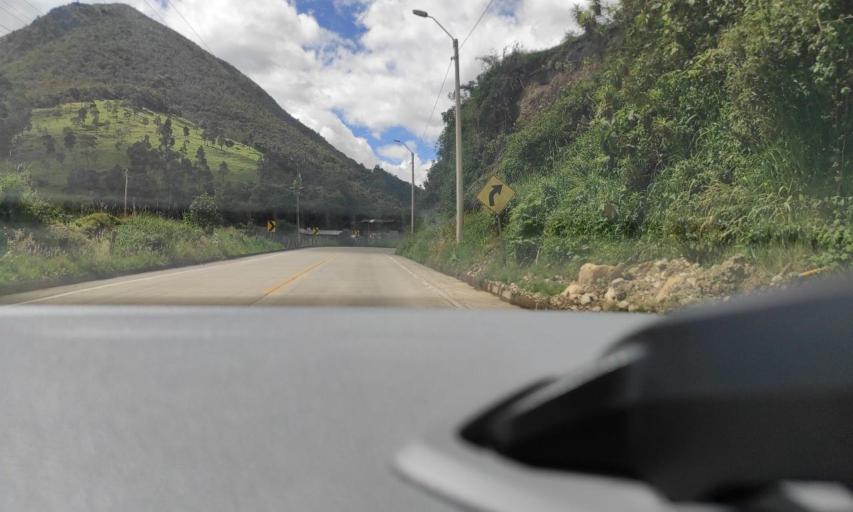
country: EC
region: Azuay
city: Cuenca
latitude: -2.8408
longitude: -79.1243
